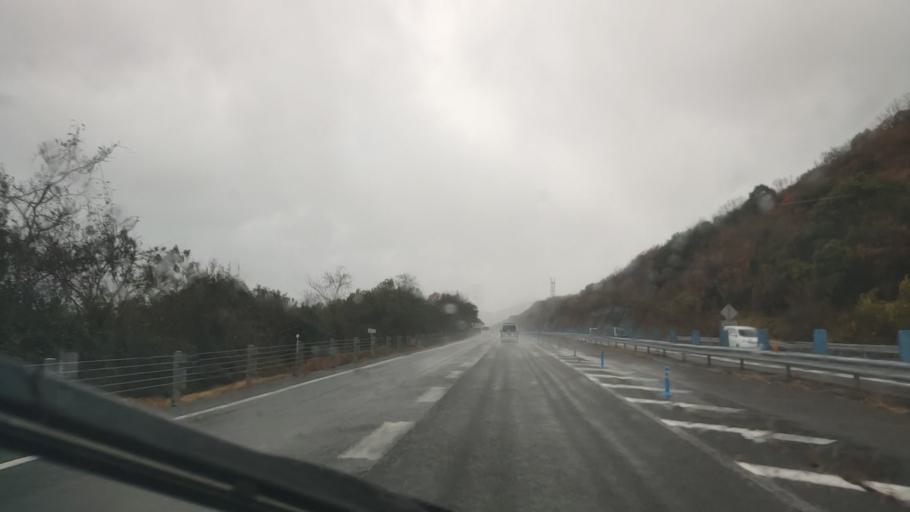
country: JP
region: Tokushima
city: Kamojimacho-jogejima
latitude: 34.1064
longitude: 134.2562
